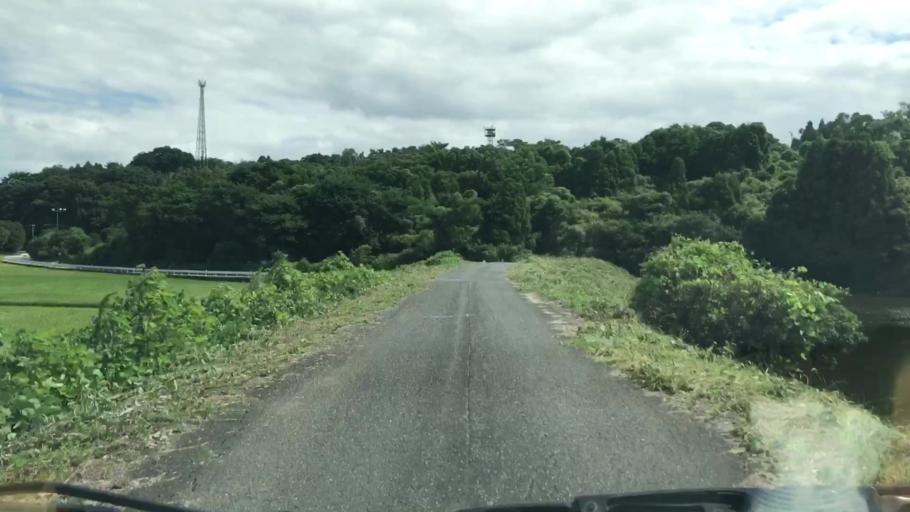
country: JP
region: Saga Prefecture
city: Saga-shi
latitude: 33.2319
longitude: 130.1734
